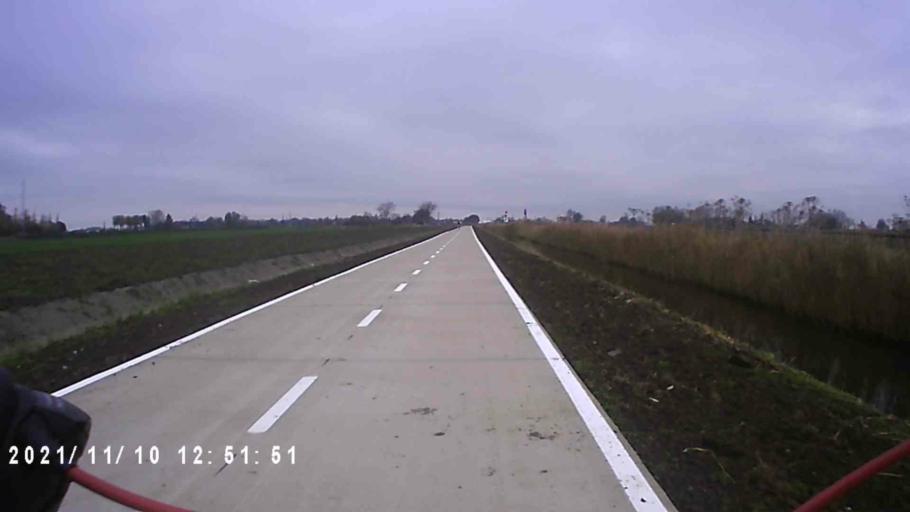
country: NL
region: Groningen
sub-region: Gemeente Winsum
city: Winsum
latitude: 53.2801
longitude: 6.5395
